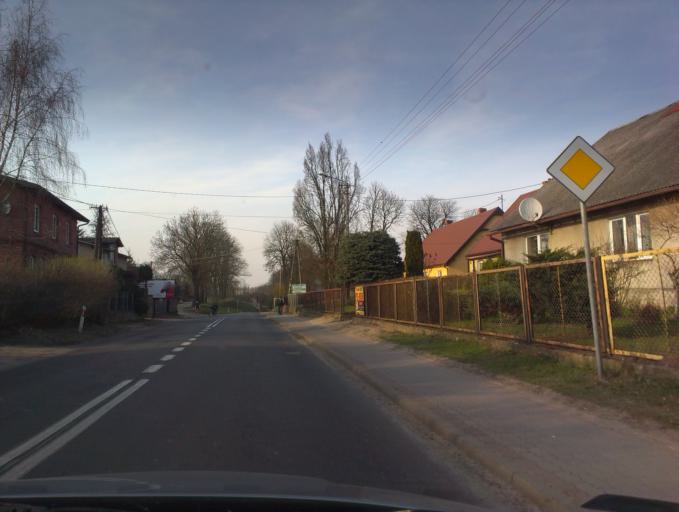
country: PL
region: Pomeranian Voivodeship
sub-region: Powiat czluchowski
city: Debrzno
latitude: 53.5284
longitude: 17.2313
